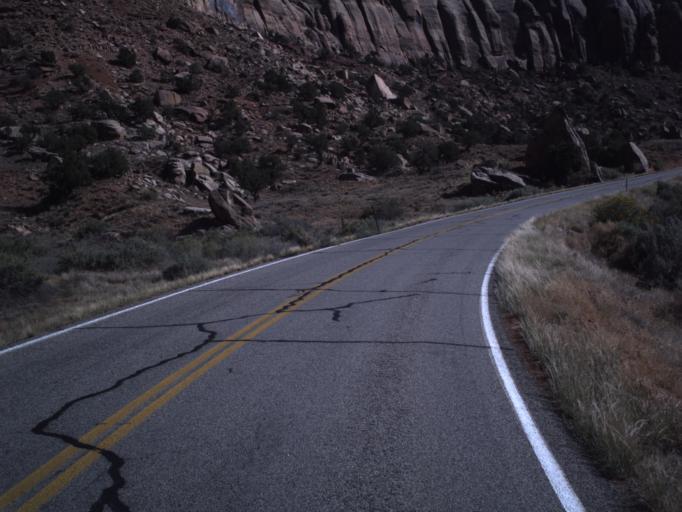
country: US
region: Utah
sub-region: San Juan County
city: Monticello
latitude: 38.0458
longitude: -109.5518
